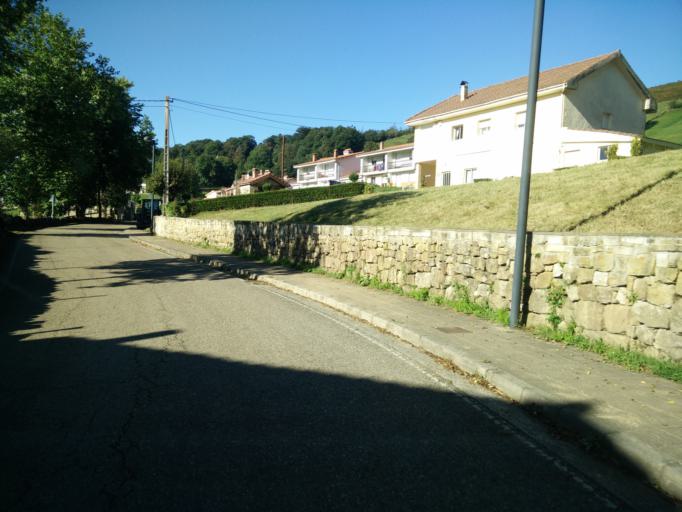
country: ES
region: Cantabria
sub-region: Provincia de Cantabria
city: San Pedro del Romeral
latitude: 43.1178
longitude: -3.8151
